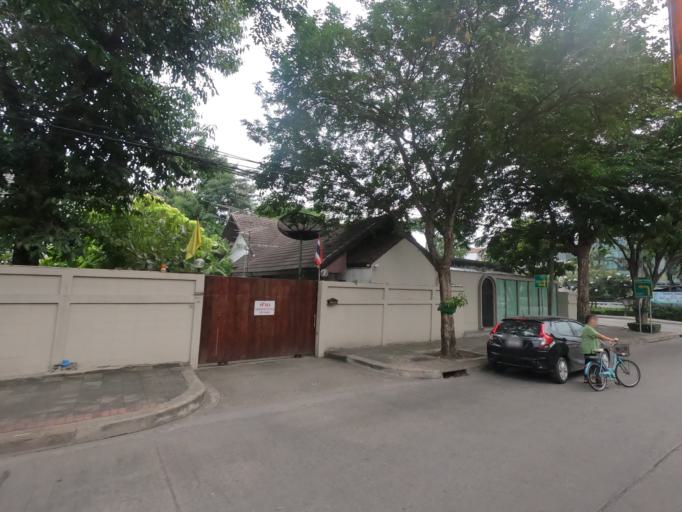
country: TH
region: Bangkok
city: Wang Thonglang
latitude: 13.7934
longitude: 100.6088
